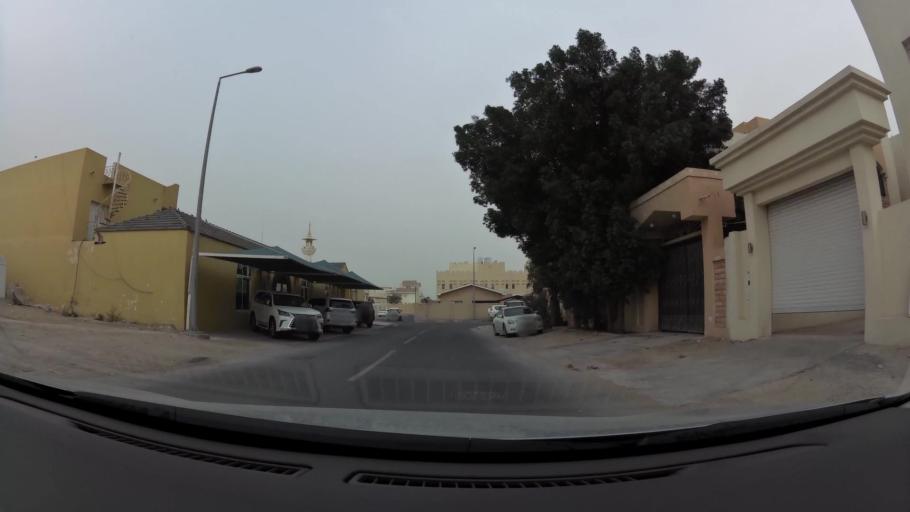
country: QA
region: Baladiyat ad Dawhah
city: Doha
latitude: 25.2492
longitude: 51.4797
